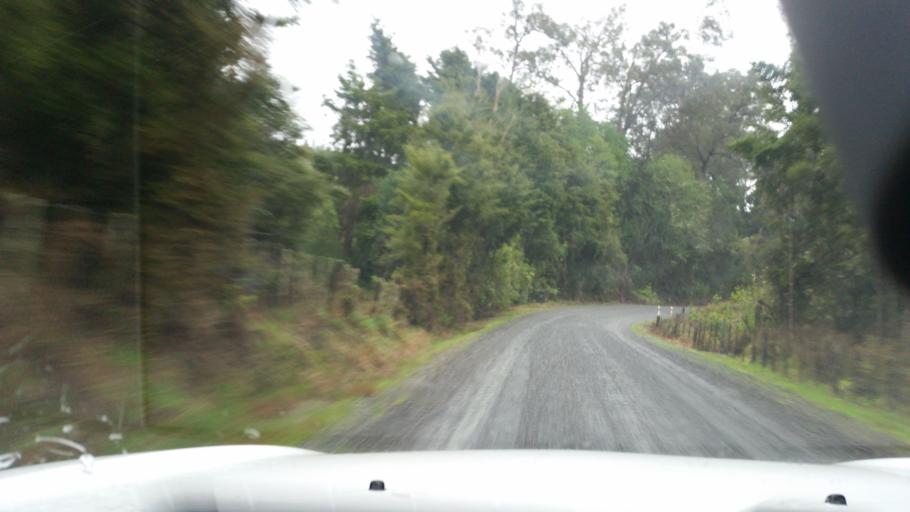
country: NZ
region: Northland
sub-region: Kaipara District
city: Dargaville
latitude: -35.7241
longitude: 173.9548
